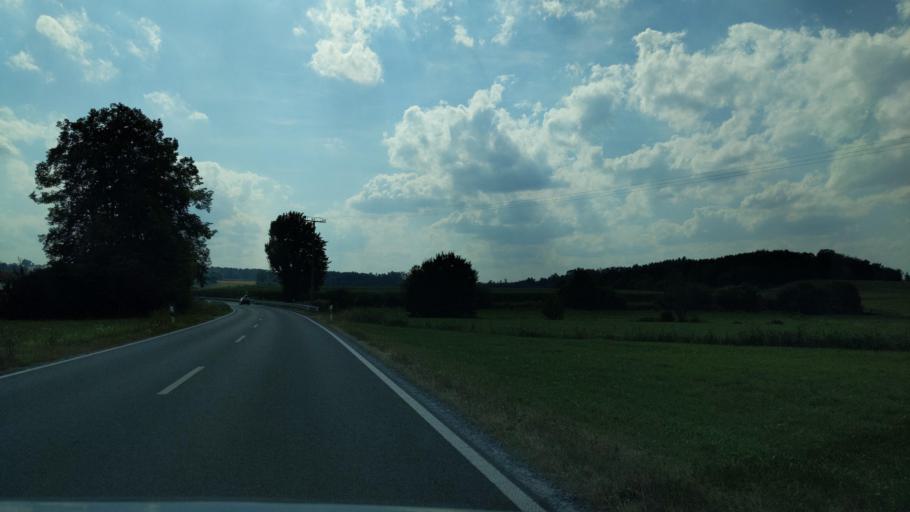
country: DE
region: Bavaria
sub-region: Upper Bavaria
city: Bruck
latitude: 48.0239
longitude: 11.9116
